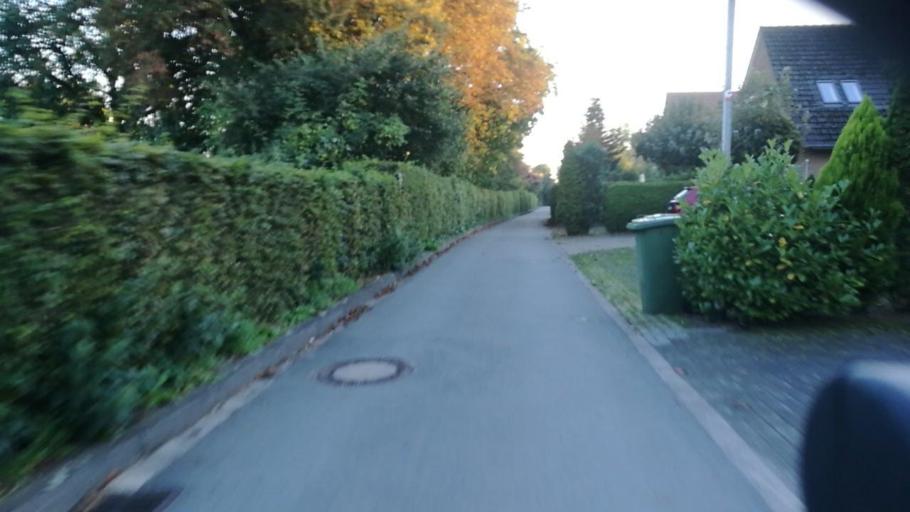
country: DE
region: North Rhine-Westphalia
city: Halle
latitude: 52.0635
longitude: 8.3648
